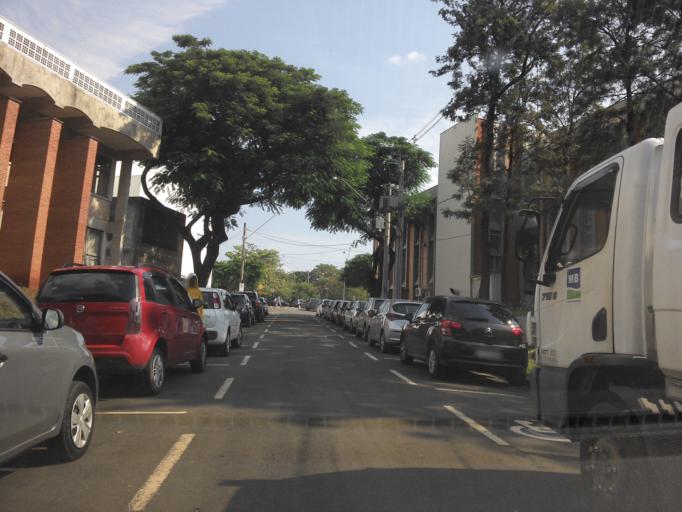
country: BR
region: Sao Paulo
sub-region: Campinas
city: Campinas
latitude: -22.8150
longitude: -47.0688
